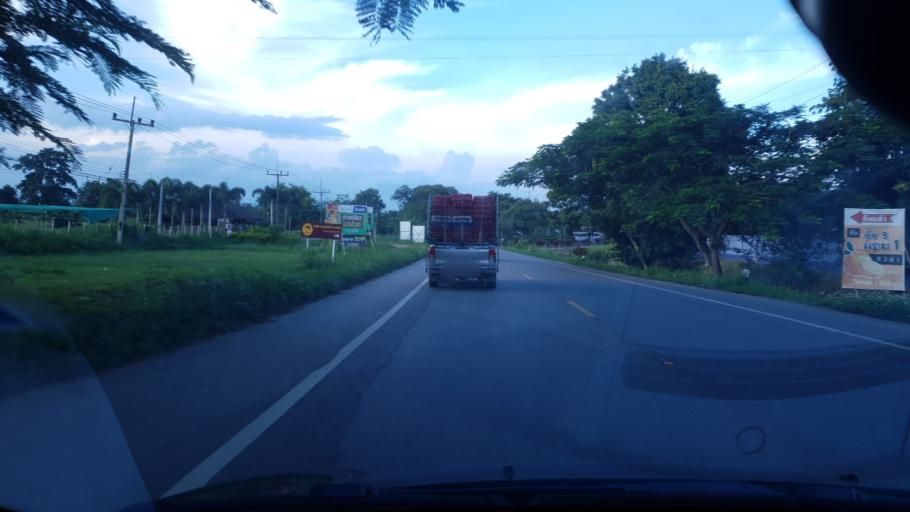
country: TH
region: Chiang Rai
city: Mae Suai
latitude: 19.5506
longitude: 99.4932
